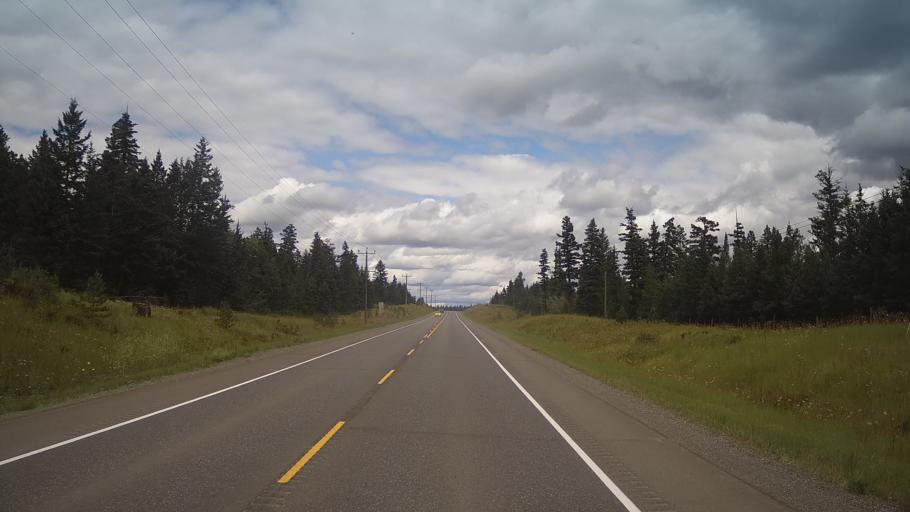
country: CA
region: British Columbia
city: Cache Creek
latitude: 51.1688
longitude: -121.5067
